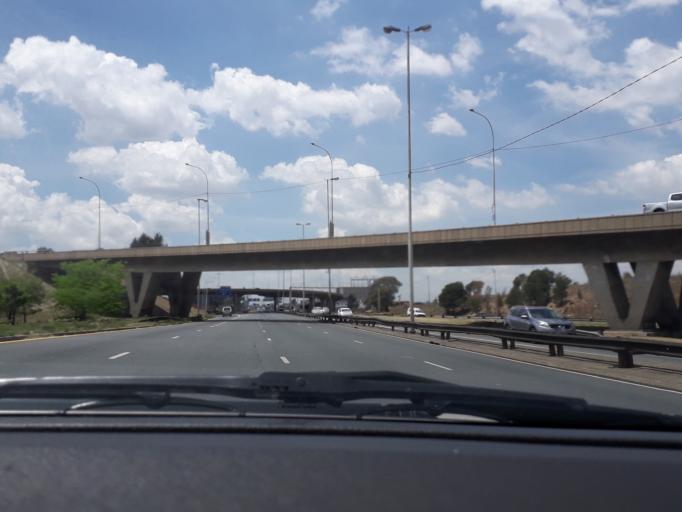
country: ZA
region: Gauteng
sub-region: City of Johannesburg Metropolitan Municipality
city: Johannesburg
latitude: -26.2121
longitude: 28.0291
